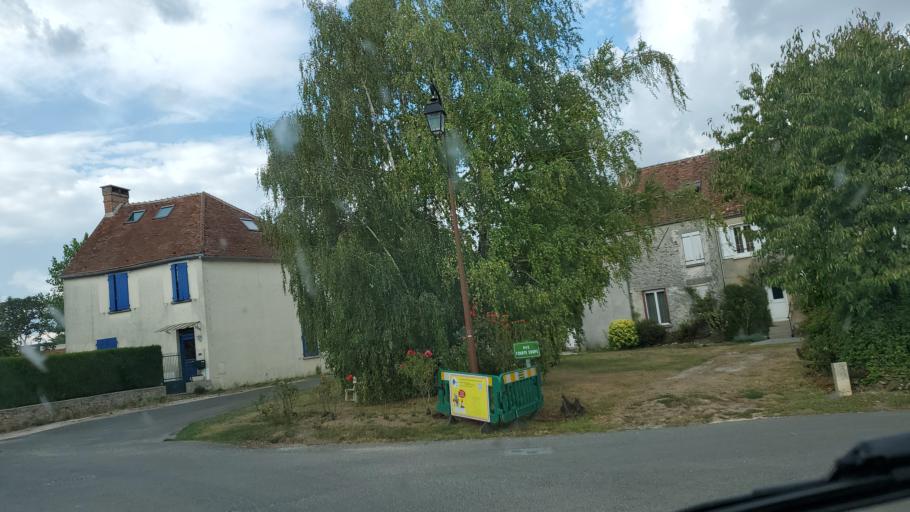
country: FR
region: Ile-de-France
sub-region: Departement de Seine-et-Marne
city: Chailly-en-Brie
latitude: 48.7778
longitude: 3.1646
